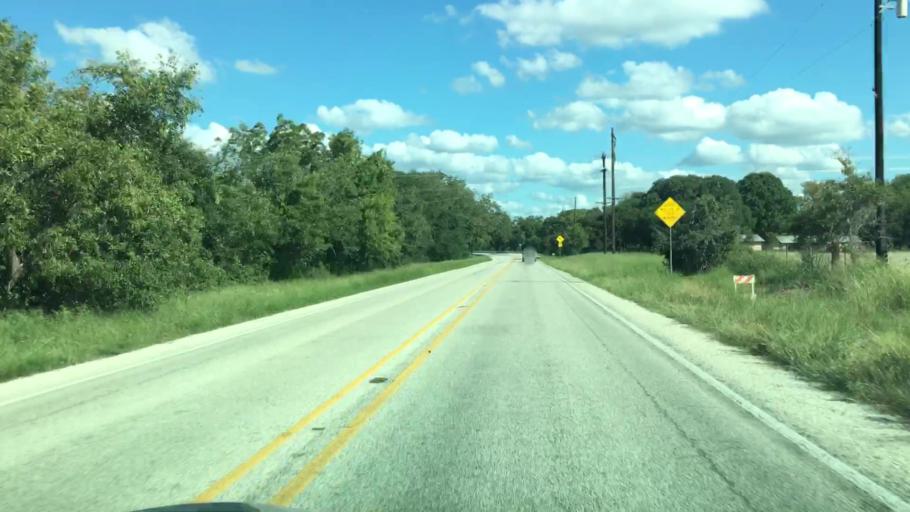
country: US
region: Texas
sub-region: Blanco County
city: Blanco
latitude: 30.0921
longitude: -98.4053
